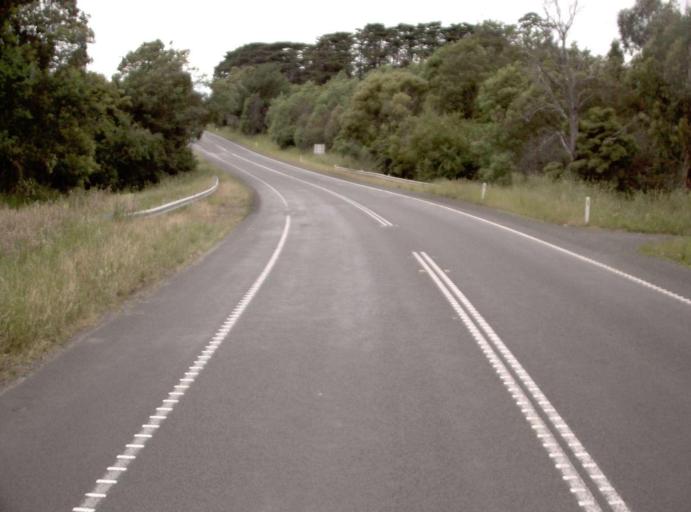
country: AU
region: Victoria
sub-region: Baw Baw
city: Warragul
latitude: -38.4471
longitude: 145.8631
